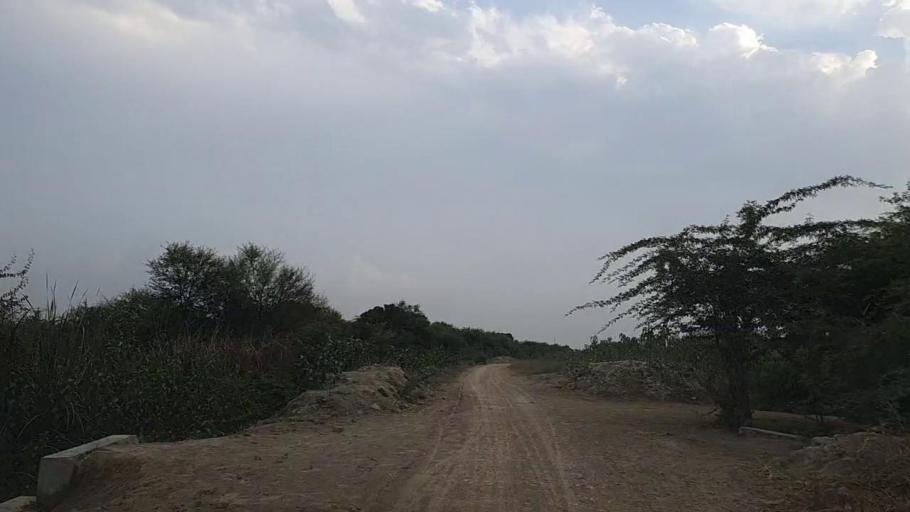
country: PK
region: Sindh
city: Daro Mehar
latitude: 24.7671
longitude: 68.1539
